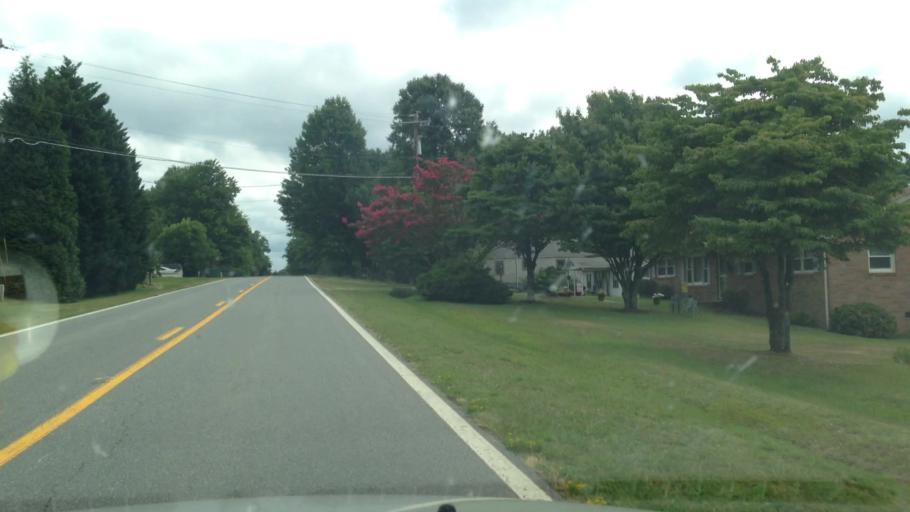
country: US
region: North Carolina
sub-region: Rockingham County
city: Reidsville
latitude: 36.4208
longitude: -79.5915
